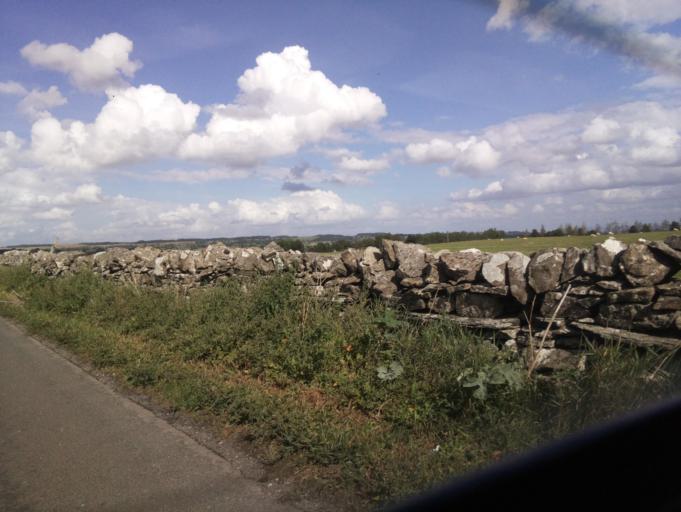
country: GB
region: England
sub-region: North Yorkshire
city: Leyburn
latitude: 54.3196
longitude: -1.8223
